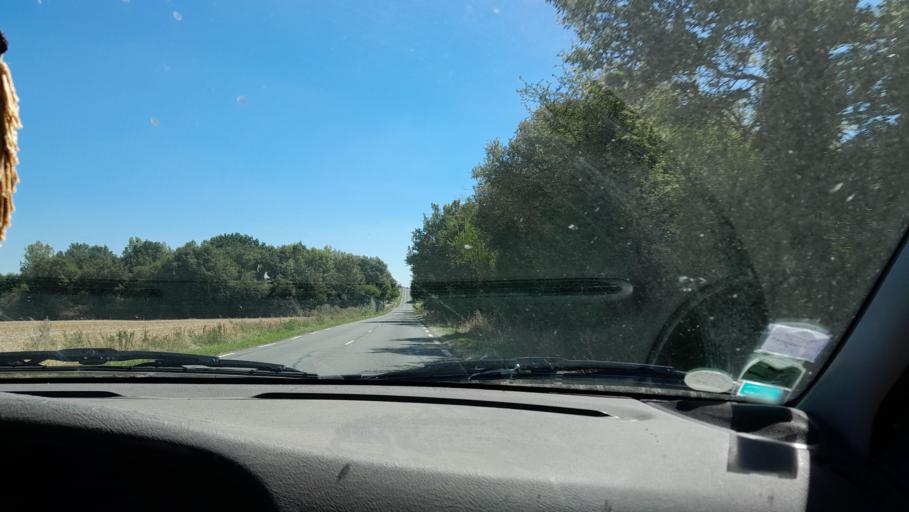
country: FR
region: Pays de la Loire
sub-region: Departement de la Loire-Atlantique
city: Saint-Mars-la-Jaille
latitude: 47.5628
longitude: -1.1865
